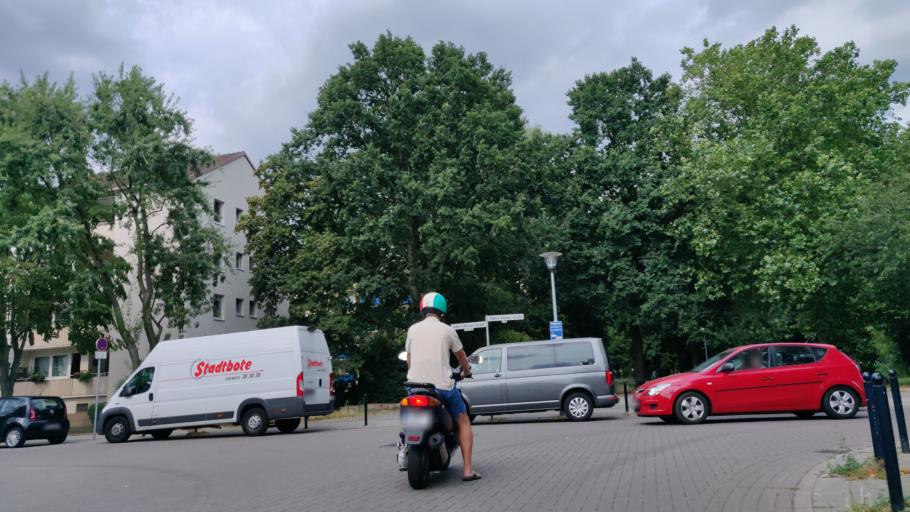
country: DE
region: Lower Saxony
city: Lilienthal
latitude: 53.1005
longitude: 8.8867
